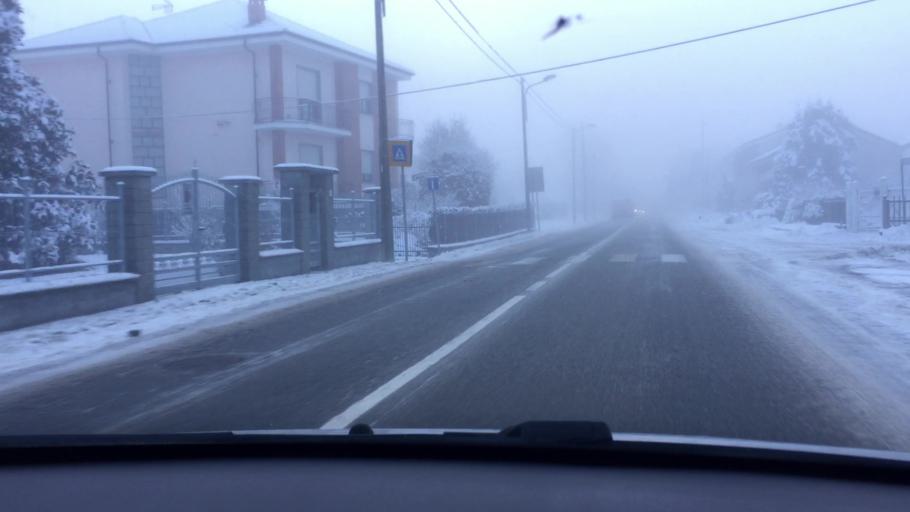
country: IT
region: Piedmont
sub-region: Provincia di Torino
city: Scalenghe
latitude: 44.8910
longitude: 7.4935
